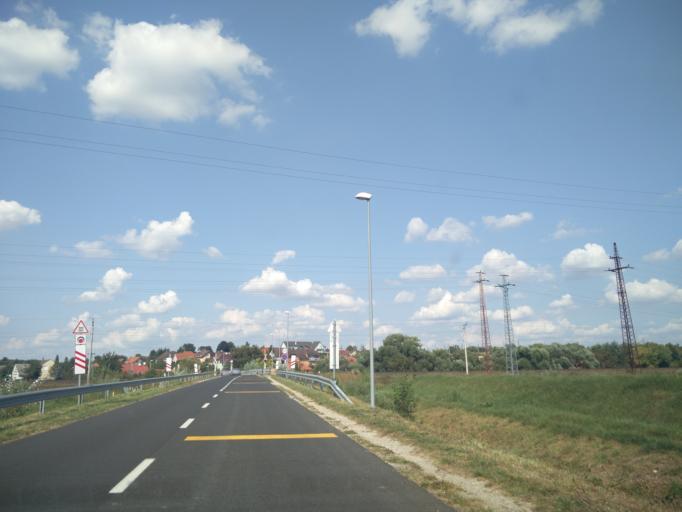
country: HU
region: Zala
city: Zalaegerszeg
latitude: 46.8533
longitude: 16.8258
